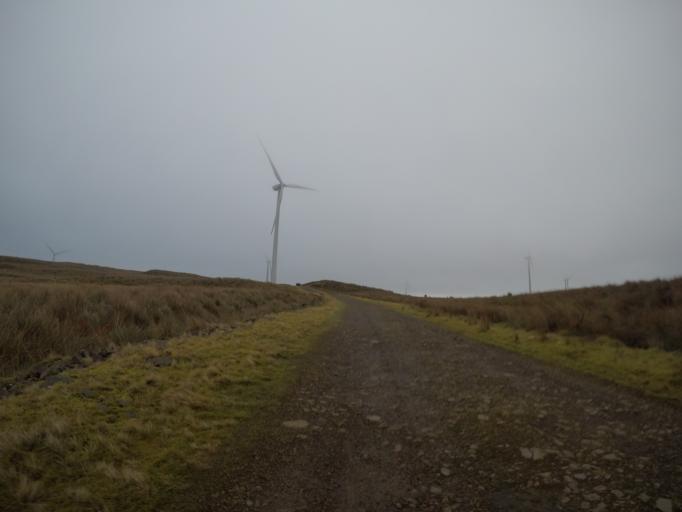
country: GB
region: Scotland
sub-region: North Ayrshire
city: Dalry
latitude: 55.7359
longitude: -4.7858
